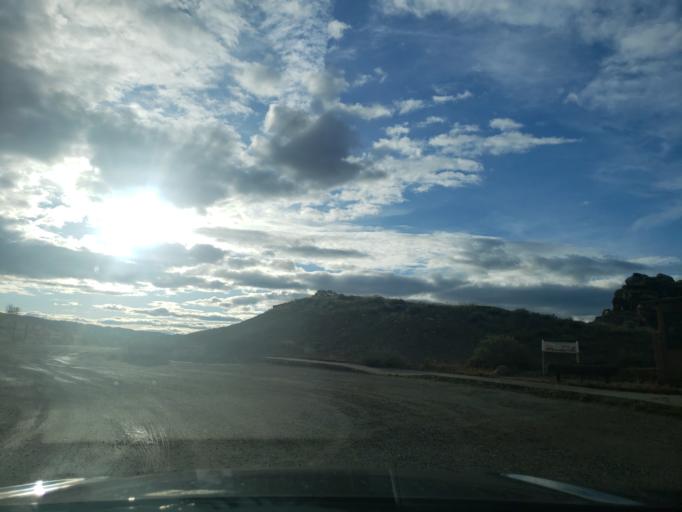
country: US
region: Colorado
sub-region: Mesa County
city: Fruita
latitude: 39.1330
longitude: -108.7364
